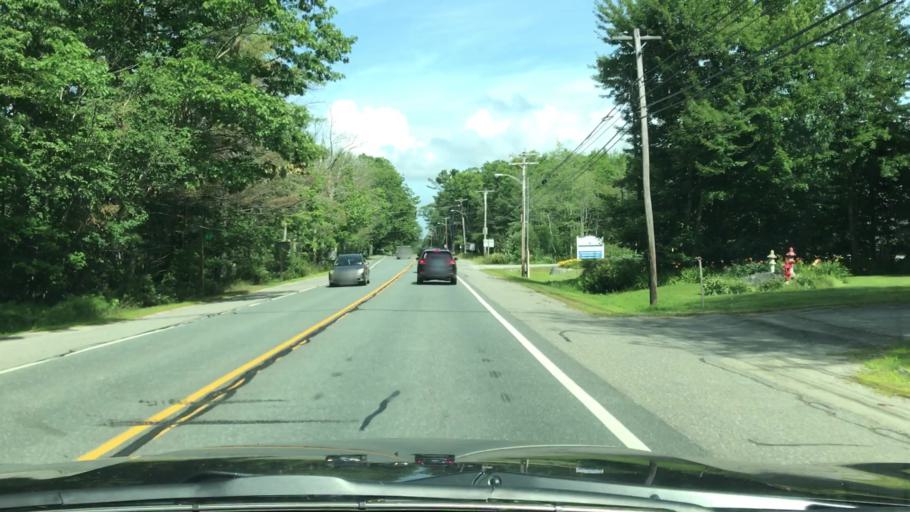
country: US
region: Maine
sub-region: Hancock County
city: Ellsworth
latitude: 44.5391
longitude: -68.4393
